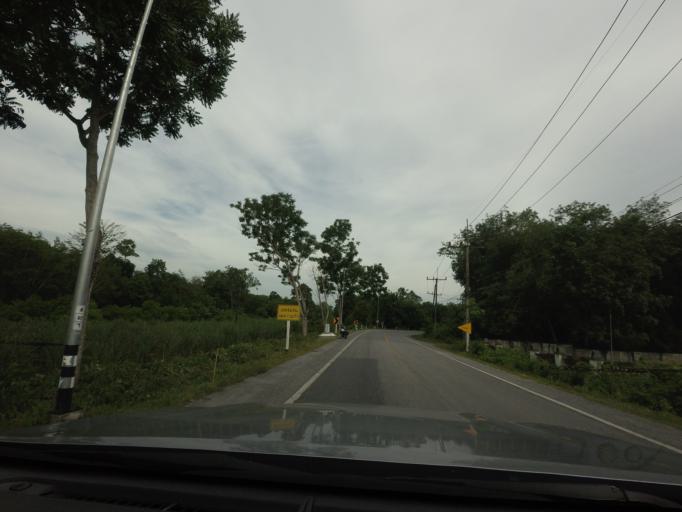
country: TH
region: Yala
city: Raman
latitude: 6.4496
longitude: 101.4512
